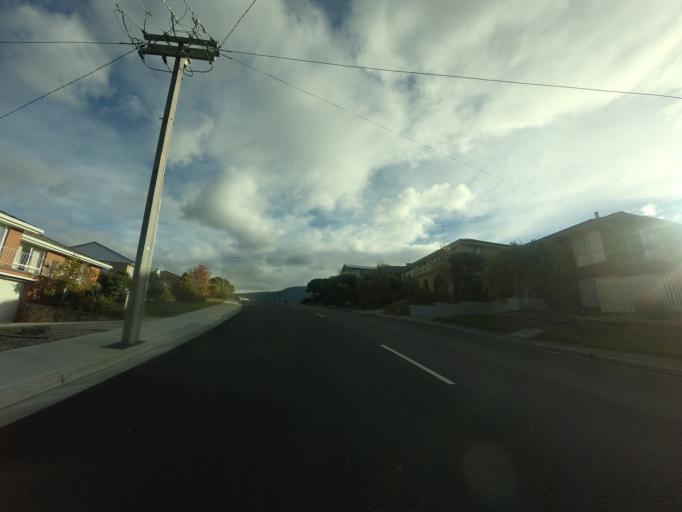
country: AU
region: Tasmania
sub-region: Glenorchy
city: Austins Ferry
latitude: -42.7722
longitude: 147.2461
